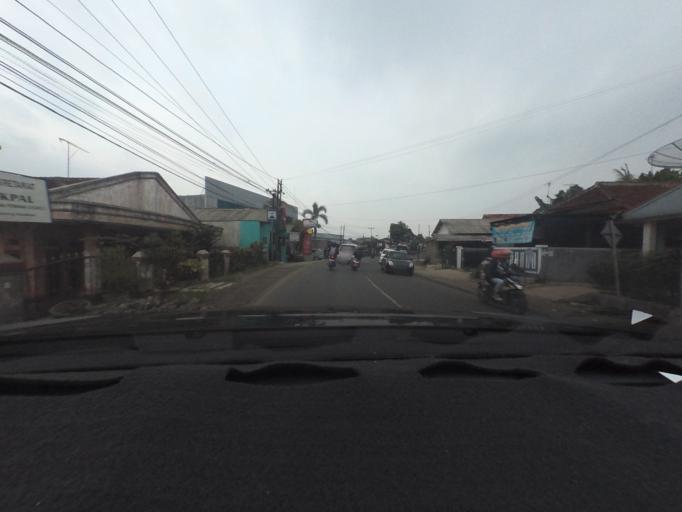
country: ID
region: West Java
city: Cicurug
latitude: -6.8007
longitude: 106.7747
